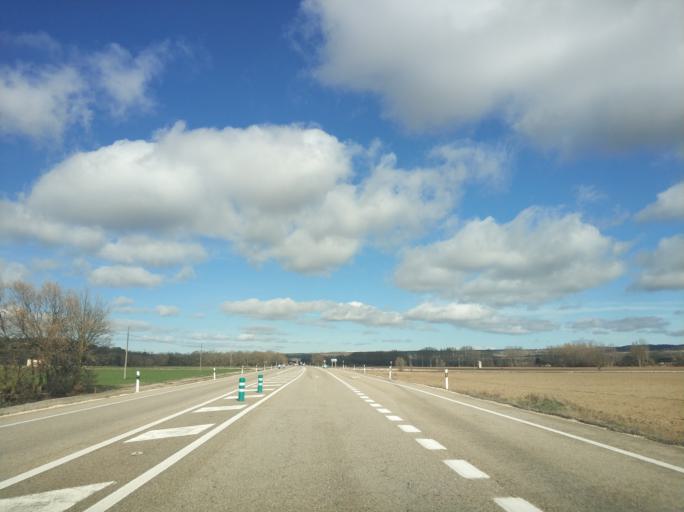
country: ES
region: Castille and Leon
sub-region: Provincia de Burgos
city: Sarracin
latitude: 42.2418
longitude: -3.6746
